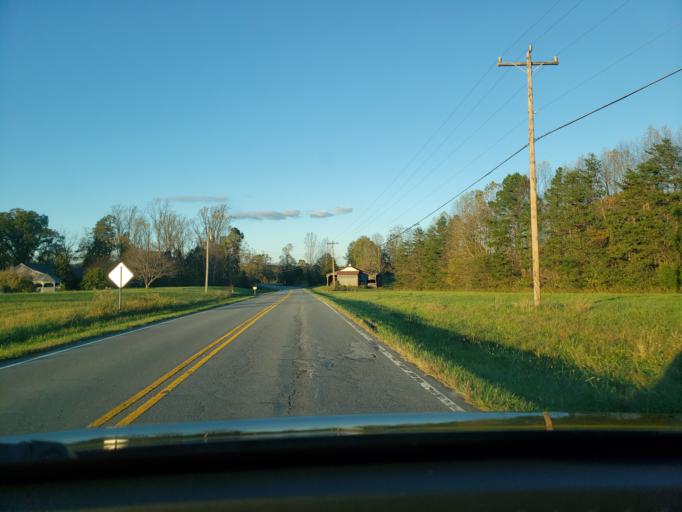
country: US
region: North Carolina
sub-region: Stokes County
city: Danbury
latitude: 36.3264
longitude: -80.2260
